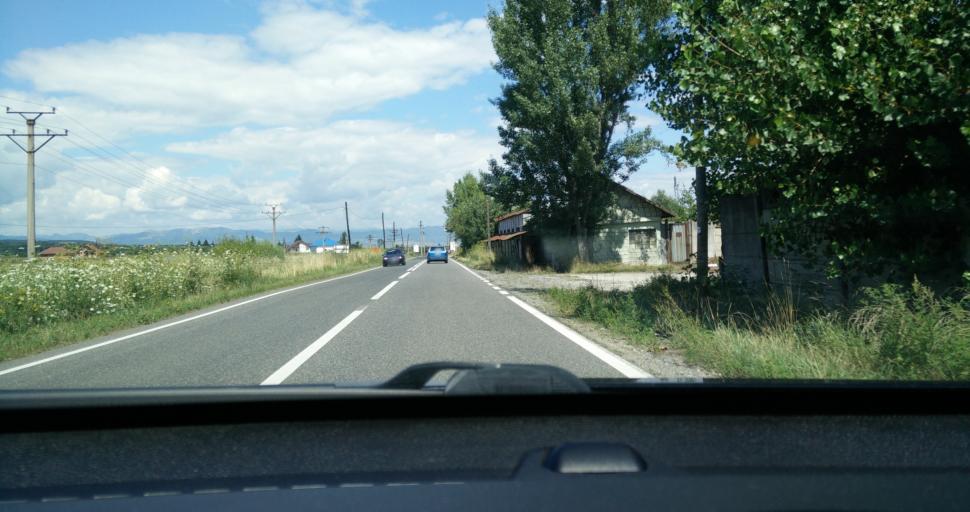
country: RO
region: Alba
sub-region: Comuna Sasciori
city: Sebesel
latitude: 45.9033
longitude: 23.5573
